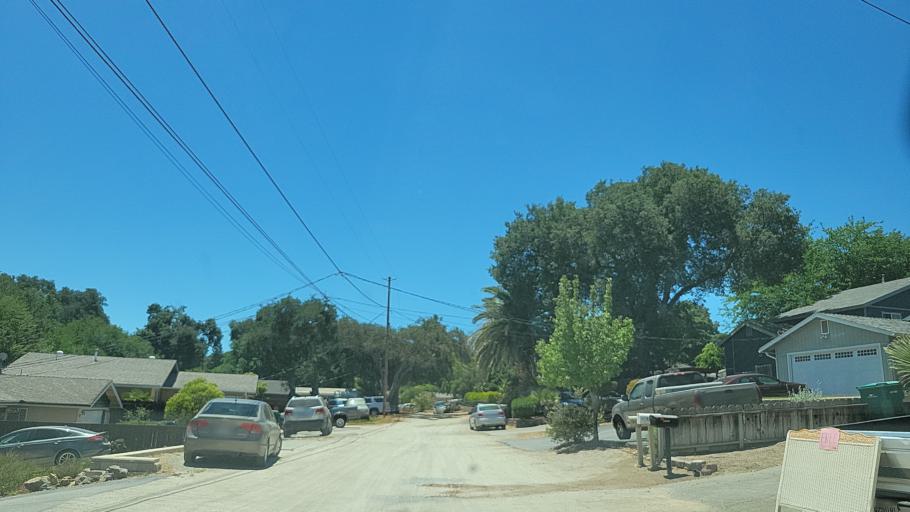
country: US
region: California
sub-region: San Luis Obispo County
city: Atascadero
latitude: 35.5075
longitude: -120.6724
